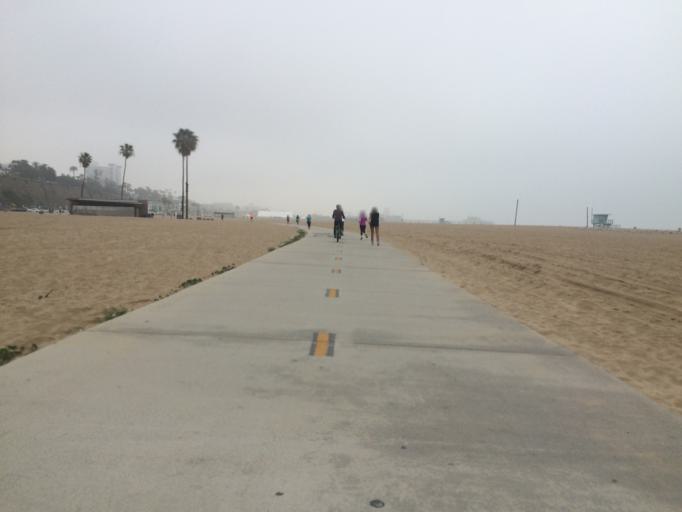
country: US
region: California
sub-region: Los Angeles County
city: Santa Monica
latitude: 34.0177
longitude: -118.5056
